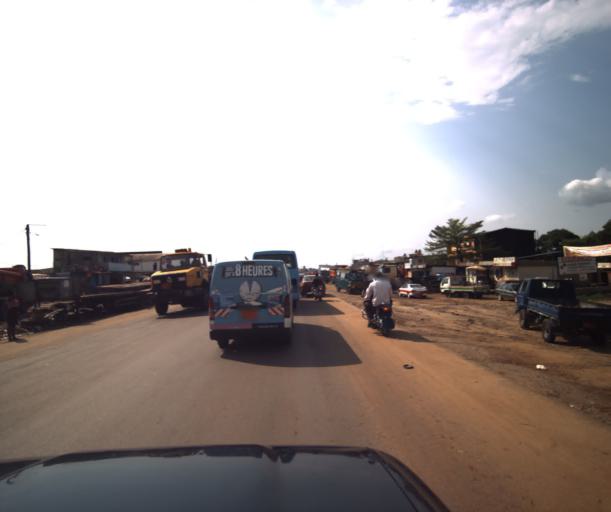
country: CM
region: Littoral
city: Douala
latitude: 4.0133
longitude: 9.7299
